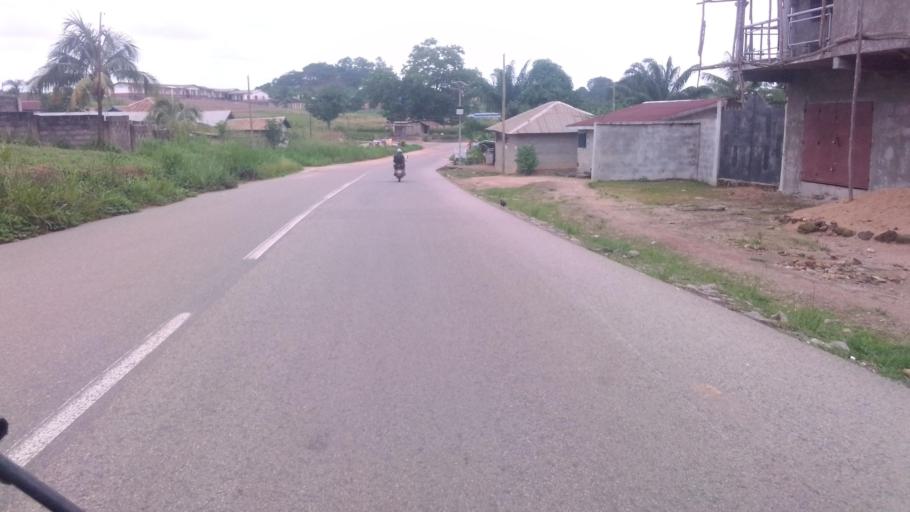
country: SL
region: Eastern Province
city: Kenema
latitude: 7.8774
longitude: -11.1677
